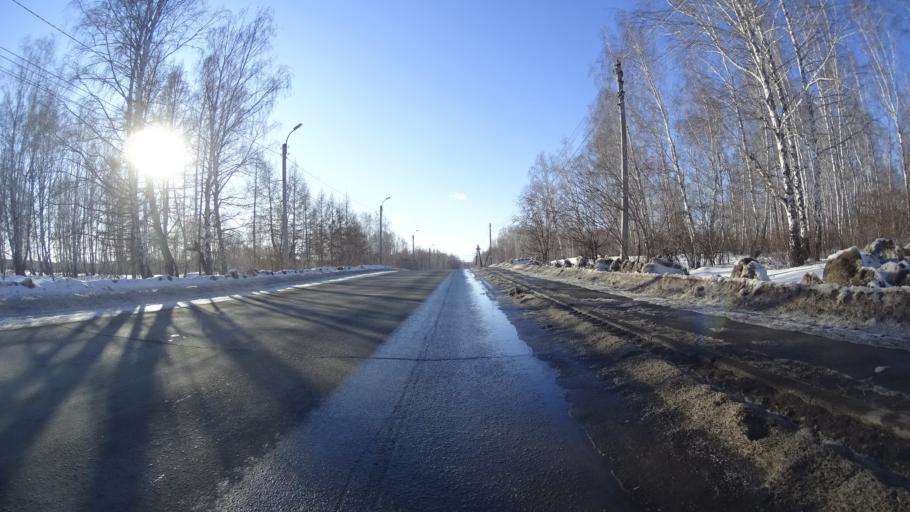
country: RU
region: Chelyabinsk
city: Sargazy
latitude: 55.1490
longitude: 61.2886
